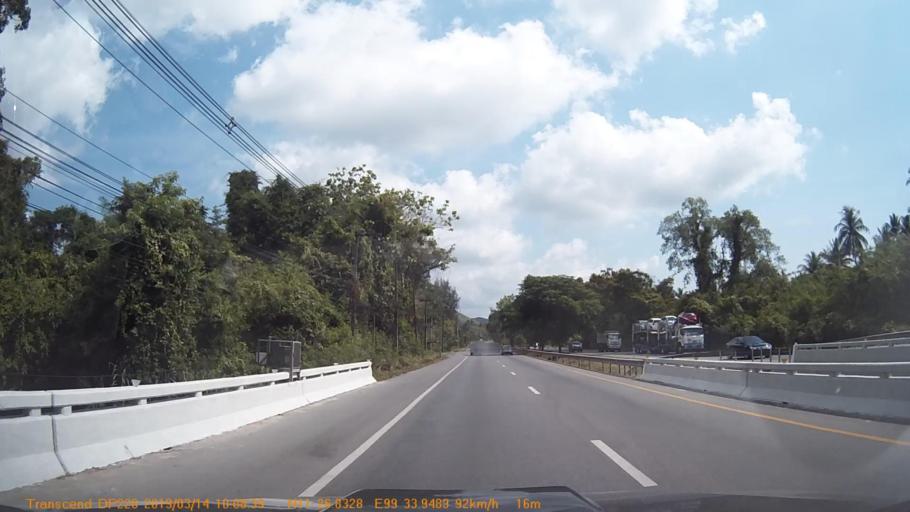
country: TH
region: Prachuap Khiri Khan
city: Thap Sakae
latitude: 11.4466
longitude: 99.5656
